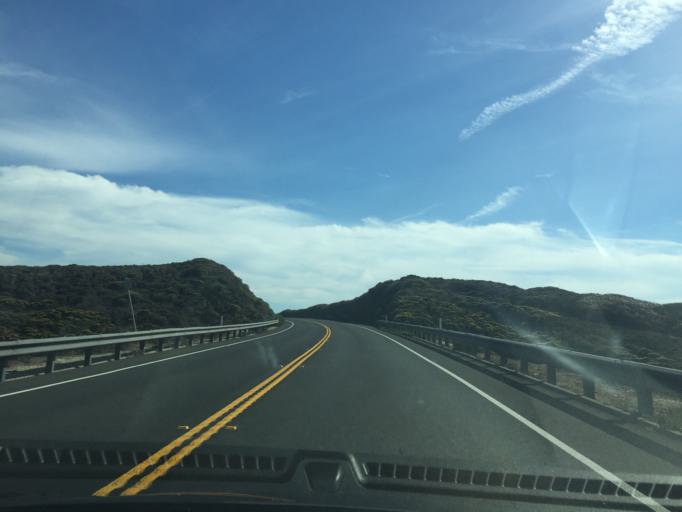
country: US
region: California
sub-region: Santa Cruz County
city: Bonny Doon
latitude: 37.0368
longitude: -122.2265
